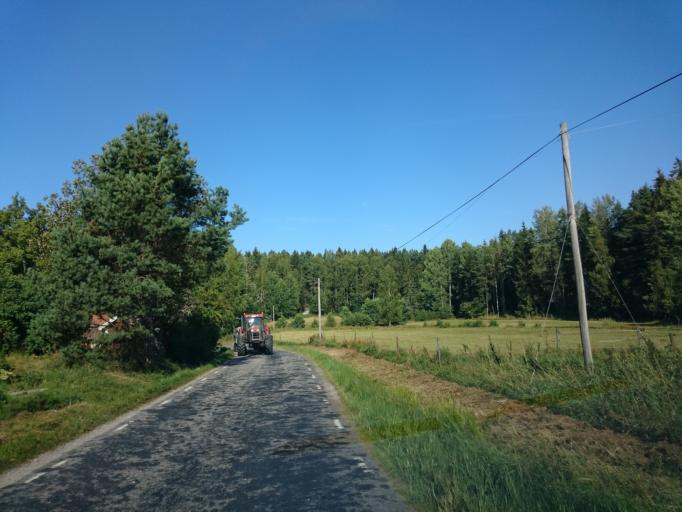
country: SE
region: Soedermanland
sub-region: Nykopings Kommun
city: Svalsta
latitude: 58.6322
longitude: 16.7653
